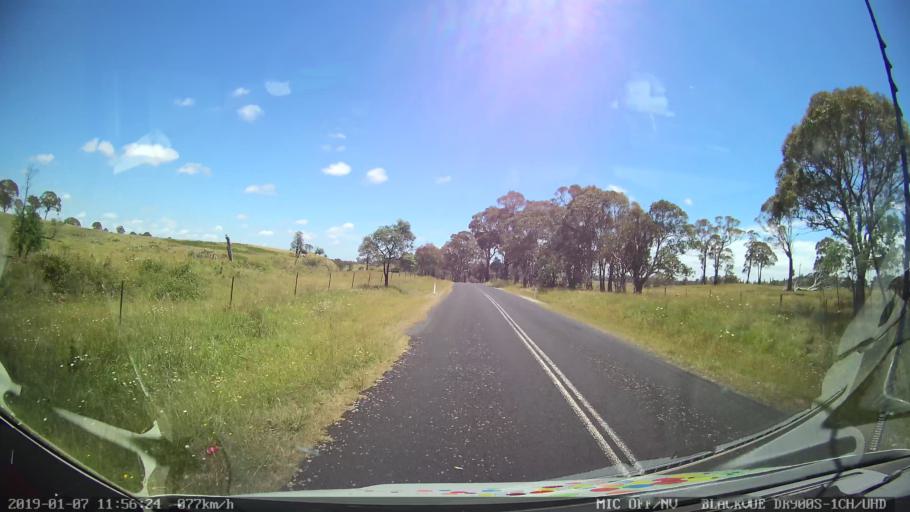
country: AU
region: New South Wales
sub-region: Guyra
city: Guyra
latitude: -30.2750
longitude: 151.6738
